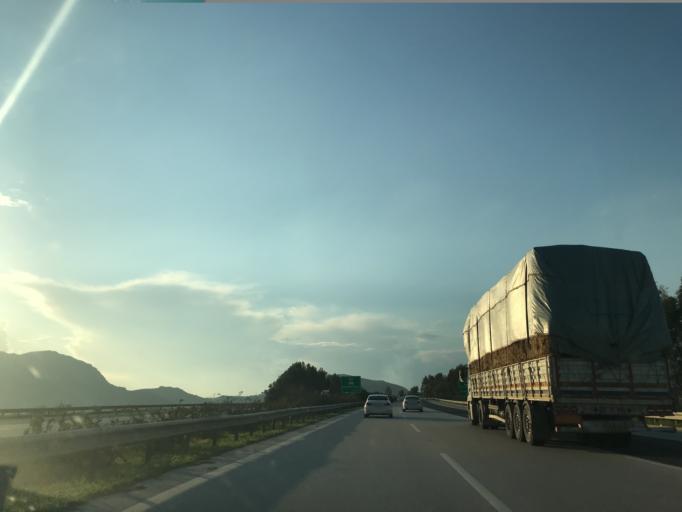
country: TR
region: Adana
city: Ceyhan
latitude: 36.9835
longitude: 35.7737
